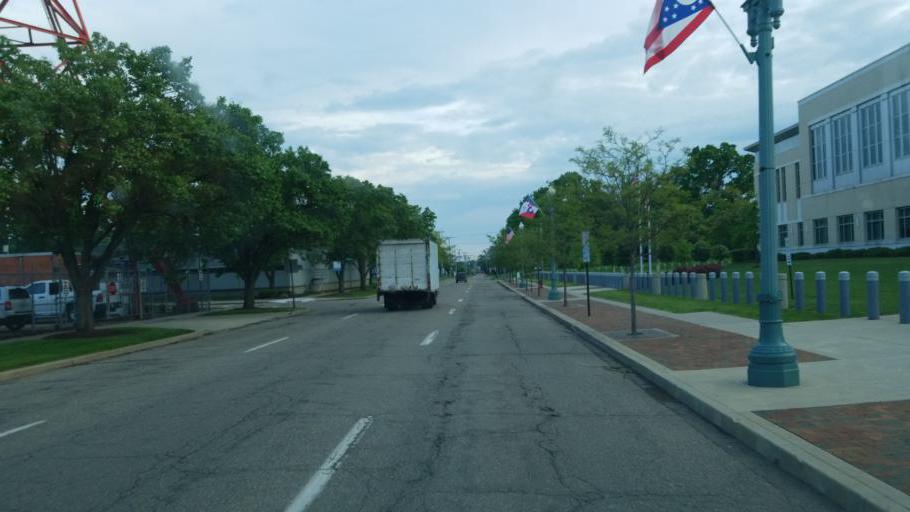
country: US
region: Ohio
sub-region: Stark County
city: Canton
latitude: 40.7975
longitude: -81.3790
